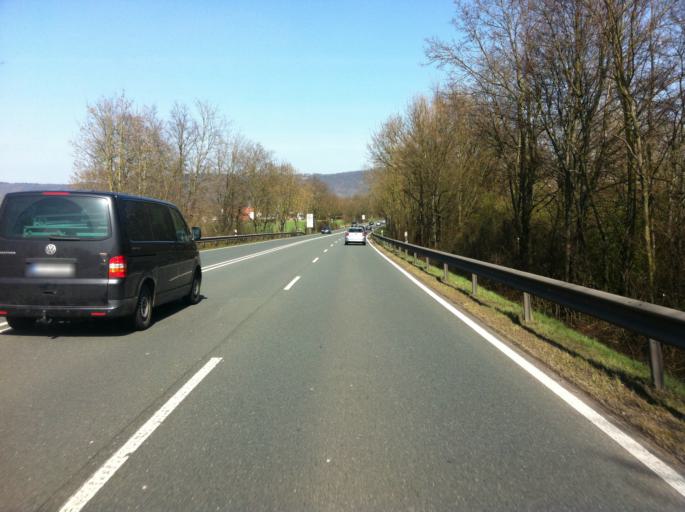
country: DE
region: North Rhine-Westphalia
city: Porta Westfalica
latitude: 52.2152
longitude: 8.8769
